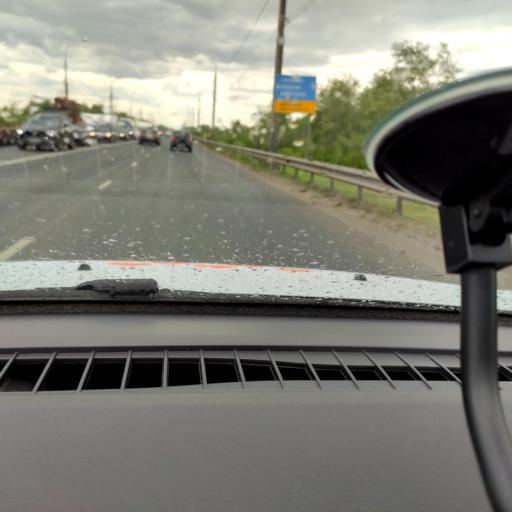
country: RU
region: Samara
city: Samara
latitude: 53.1637
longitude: 50.1944
